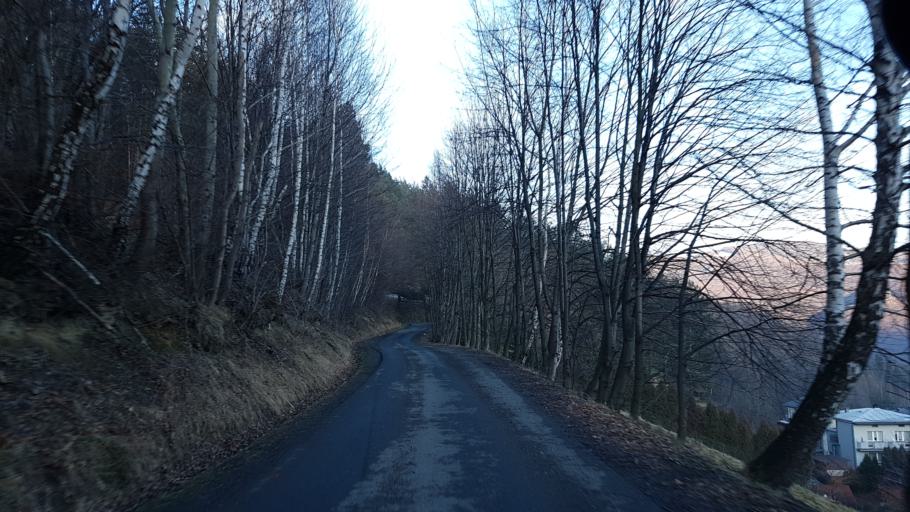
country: PL
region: Lesser Poland Voivodeship
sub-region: Powiat nowosadecki
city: Rytro
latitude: 49.4908
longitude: 20.6627
